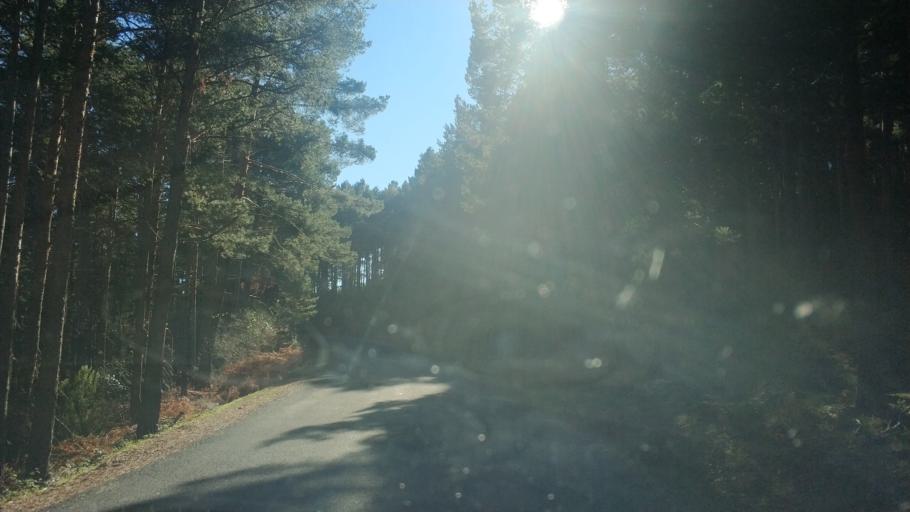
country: ES
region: Castille and Leon
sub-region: Provincia de Soria
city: Vinuesa
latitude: 41.9713
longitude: -2.7935
